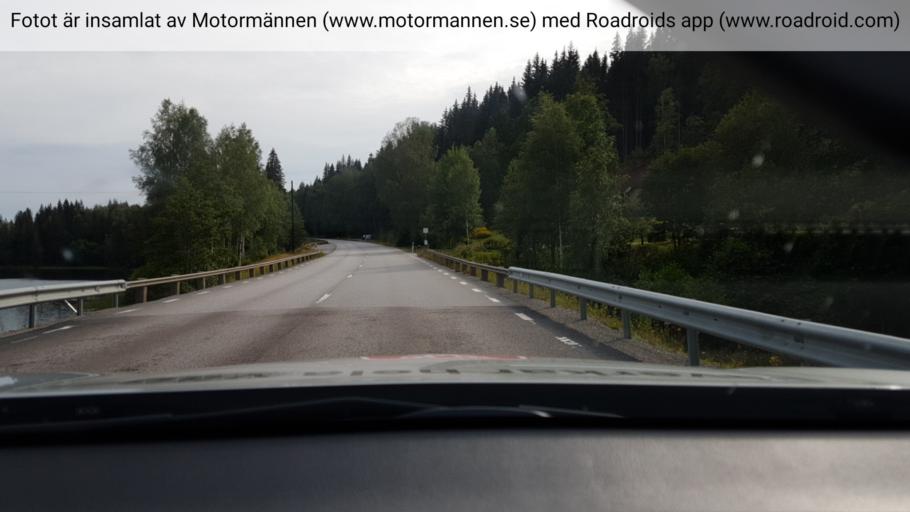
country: SE
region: Vaestra Goetaland
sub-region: Bengtsfors Kommun
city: Dals Langed
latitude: 59.0522
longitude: 12.4361
